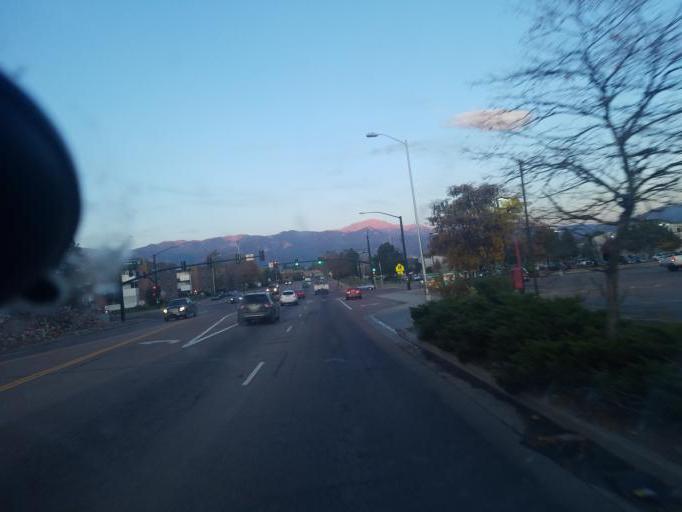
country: US
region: Colorado
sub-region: El Paso County
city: Stratmoor
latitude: 38.8152
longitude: -104.7653
